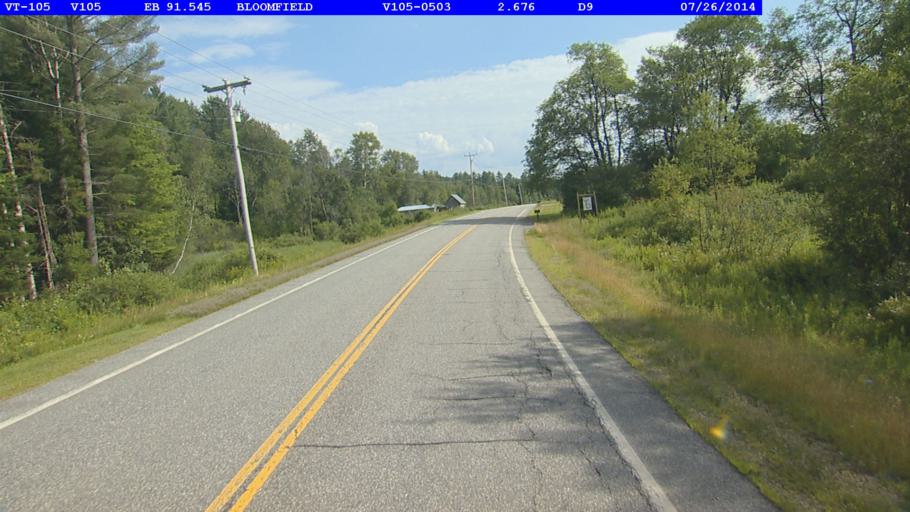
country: US
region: New Hampshire
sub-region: Coos County
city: Stratford
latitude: 44.7709
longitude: -71.6439
